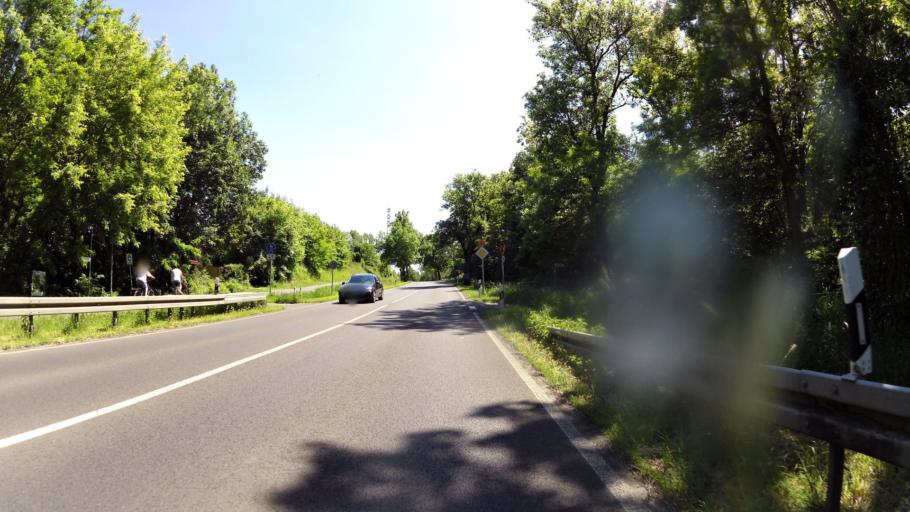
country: DE
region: Brandenburg
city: Frankfurt (Oder)
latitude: 52.3699
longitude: 14.5240
